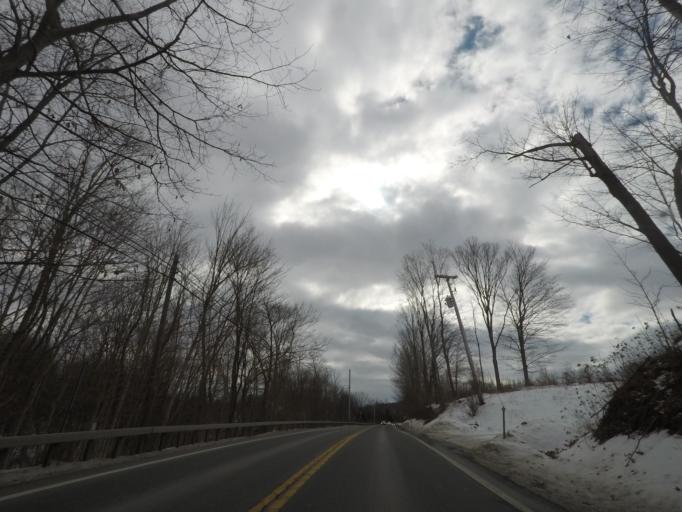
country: US
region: New York
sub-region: Washington County
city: Greenwich
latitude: 43.0779
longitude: -73.4828
